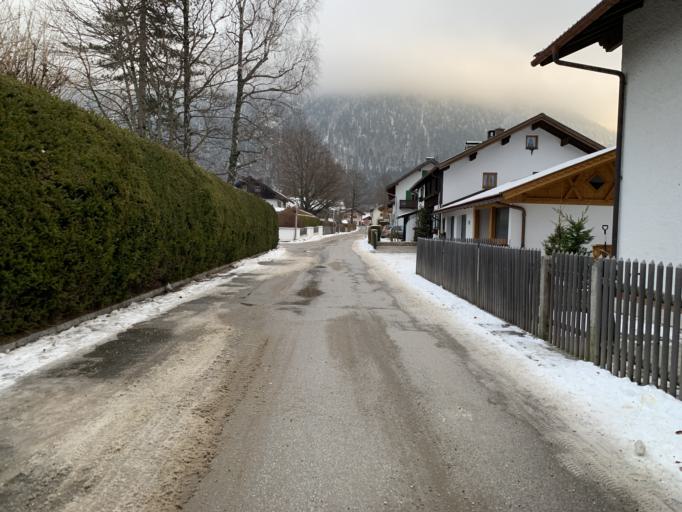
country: DE
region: Bavaria
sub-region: Upper Bavaria
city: Mittenwald
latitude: 47.4372
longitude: 11.2571
